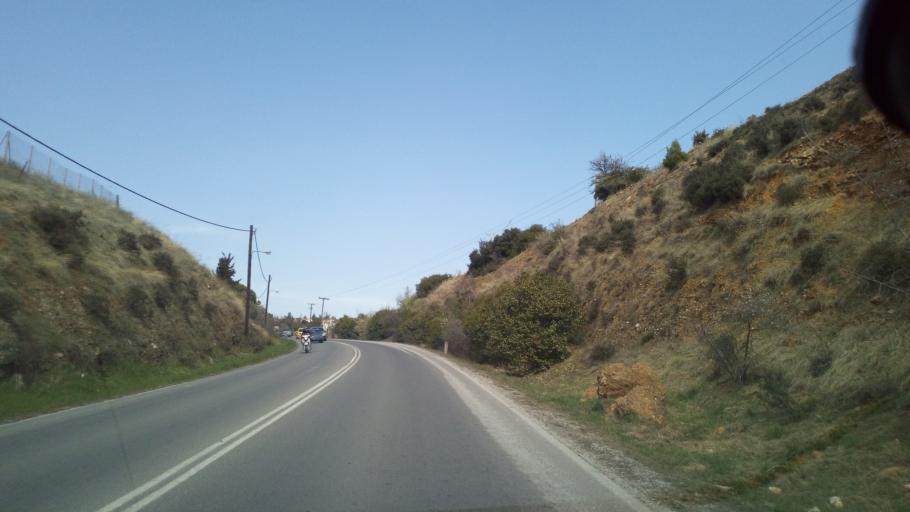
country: GR
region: Central Macedonia
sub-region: Nomos Thessalonikis
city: Panorama
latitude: 40.5702
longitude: 23.0251
